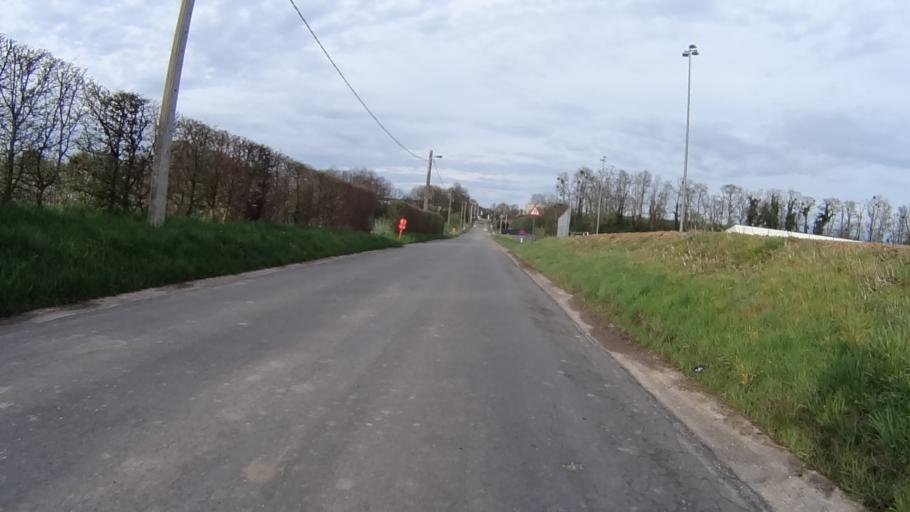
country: NL
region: Limburg
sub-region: Eijsden-Margraten
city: Eijsden
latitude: 50.7515
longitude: 5.7521
